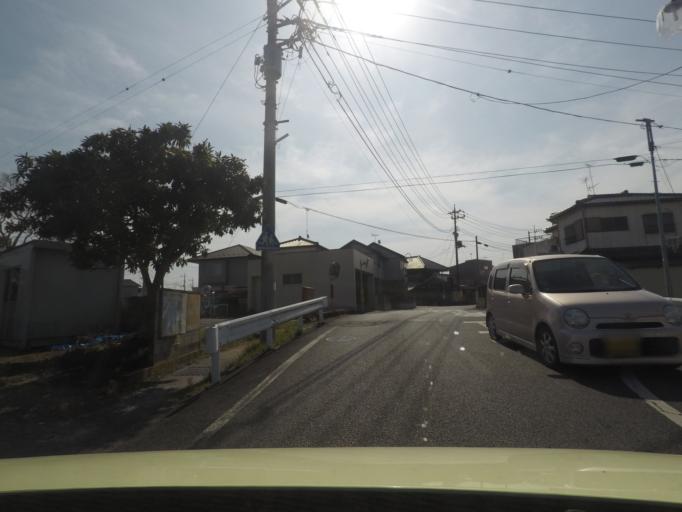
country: JP
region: Ibaraki
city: Ishioka
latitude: 36.1708
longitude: 140.3533
